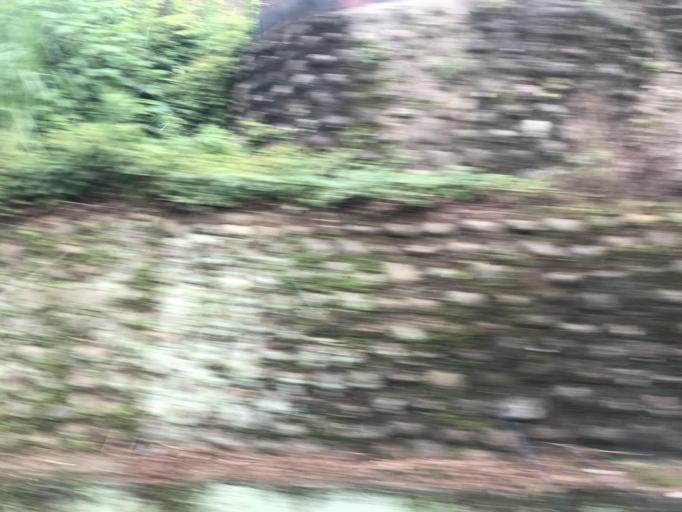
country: TW
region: Taiwan
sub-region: Taoyuan
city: Taoyuan
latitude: 24.9230
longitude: 121.3631
